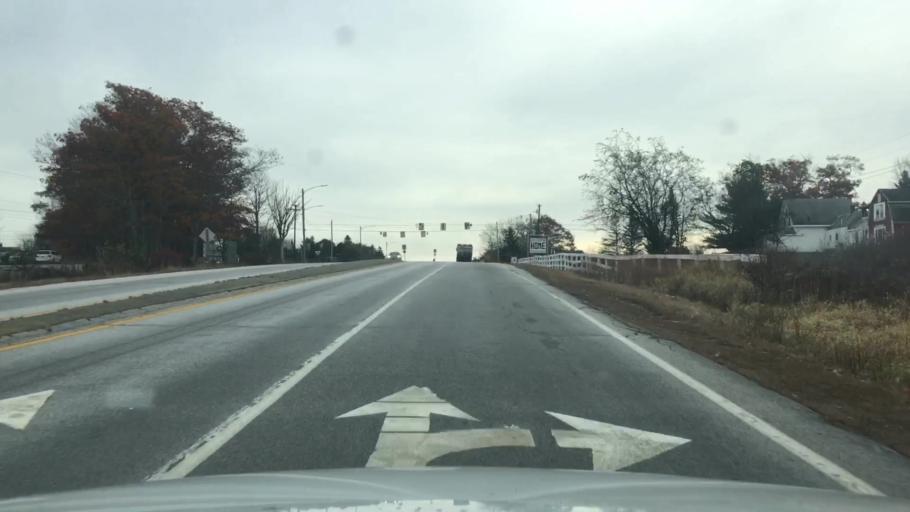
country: US
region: Maine
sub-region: Hancock County
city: Orland
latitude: 44.5746
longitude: -68.7327
